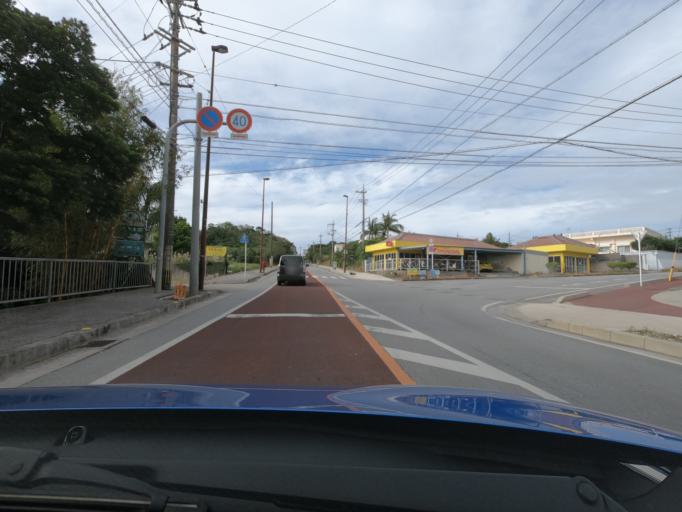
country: JP
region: Okinawa
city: Nago
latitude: 26.6789
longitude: 127.8879
